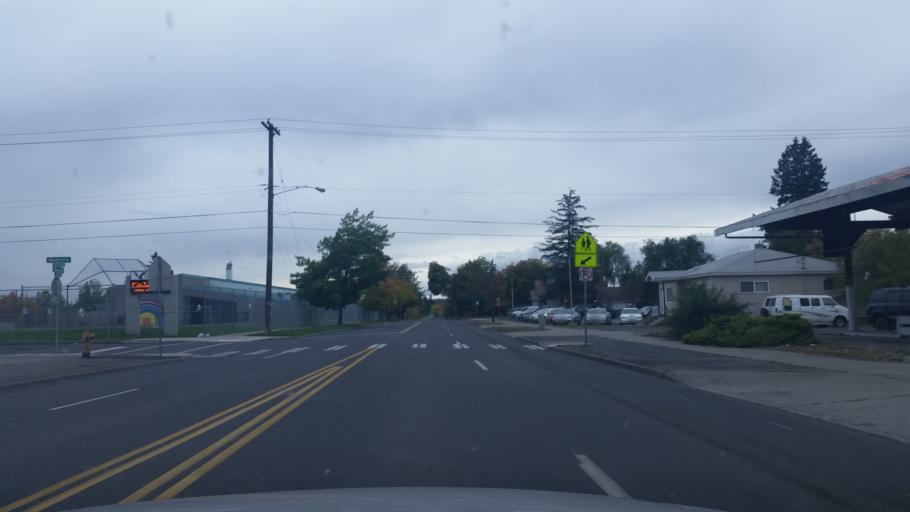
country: US
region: Washington
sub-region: Spokane County
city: Spokane
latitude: 47.6718
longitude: -117.3822
